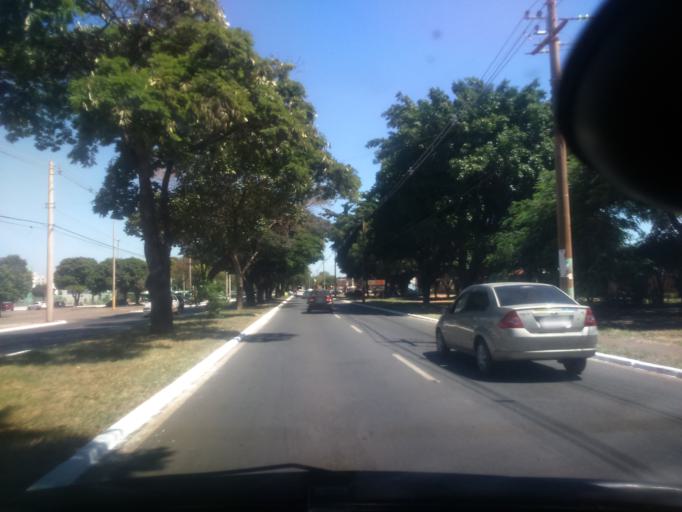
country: BR
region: Federal District
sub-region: Brasilia
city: Brasilia
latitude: -16.0103
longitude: -48.0629
